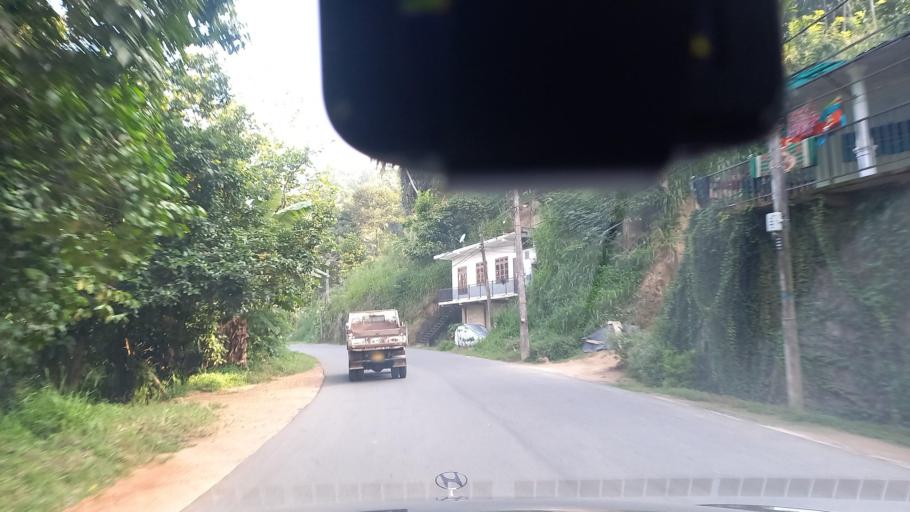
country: LK
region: Central
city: Kandy
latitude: 7.2308
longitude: 80.6032
